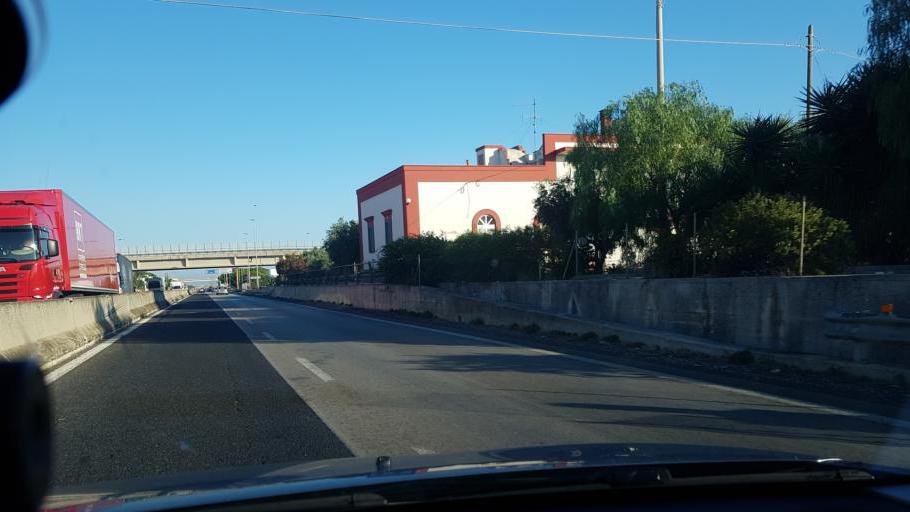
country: IT
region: Apulia
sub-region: Provincia di Brindisi
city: Fasano
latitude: 40.8785
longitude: 17.3392
